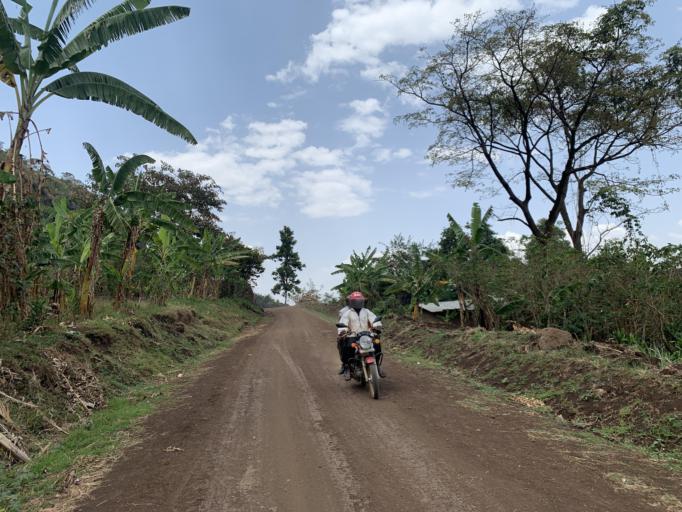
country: UG
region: Eastern Region
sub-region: Sironko District
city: Sironko
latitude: 1.2600
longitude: 34.3057
